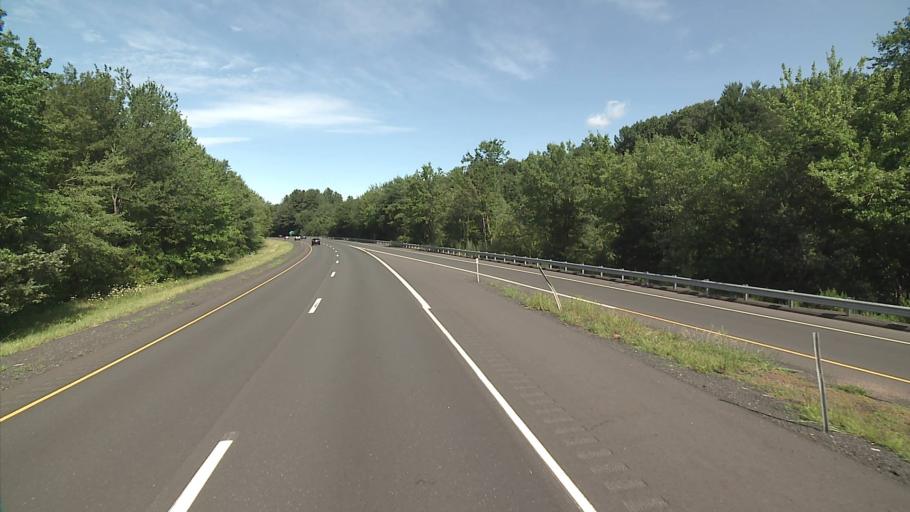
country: US
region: Connecticut
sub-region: Hartford County
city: Glastonbury Center
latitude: 41.7047
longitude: -72.5715
